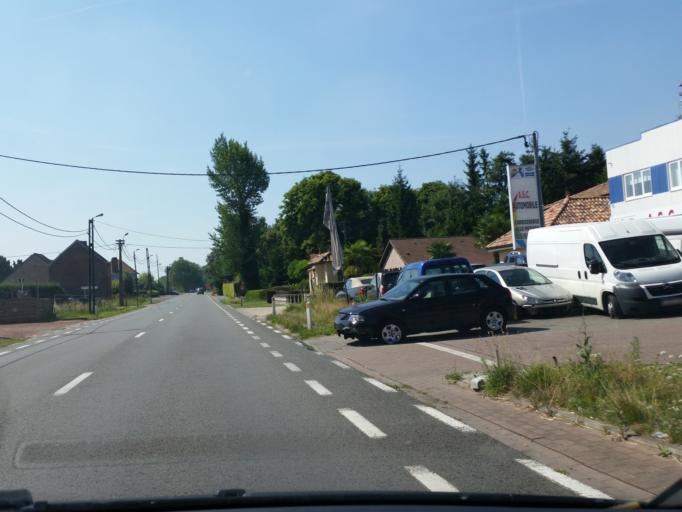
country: BE
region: Flanders
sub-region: Provincie Vlaams-Brabant
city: Steenokkerzeel
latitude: 50.9561
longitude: 4.4972
